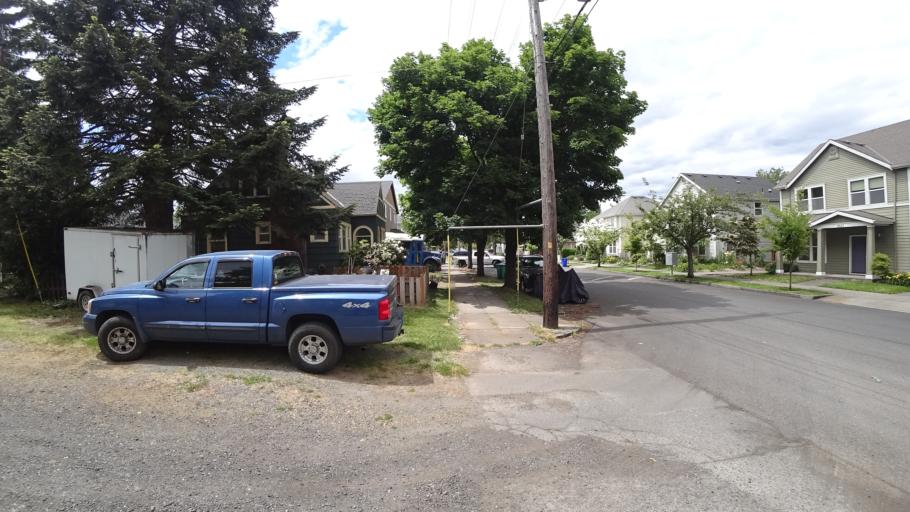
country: US
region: Oregon
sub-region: Multnomah County
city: Portland
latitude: 45.5866
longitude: -122.7154
